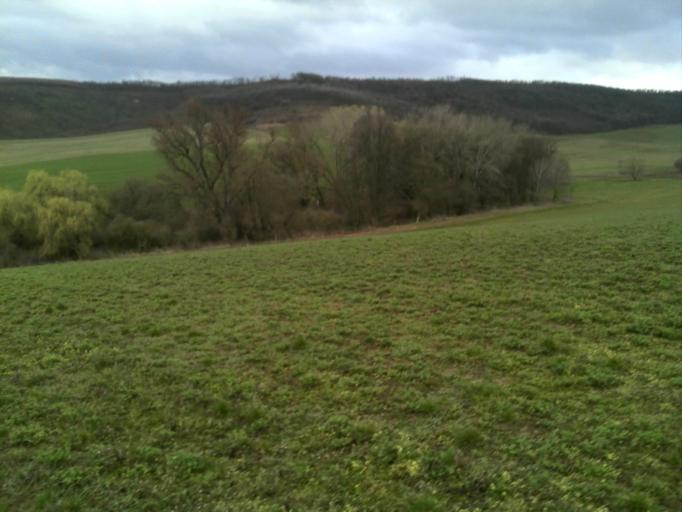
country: HU
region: Pest
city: Galgamacsa
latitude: 47.6944
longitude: 19.3526
